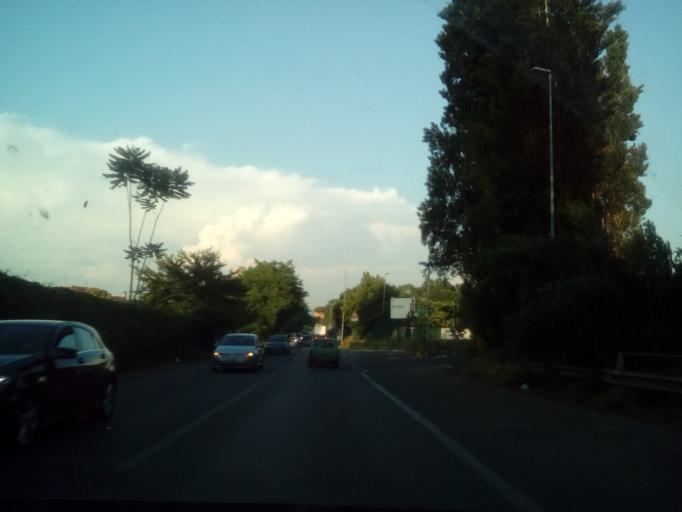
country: IT
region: Latium
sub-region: Citta metropolitana di Roma Capitale
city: Setteville
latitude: 41.9049
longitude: 12.6014
